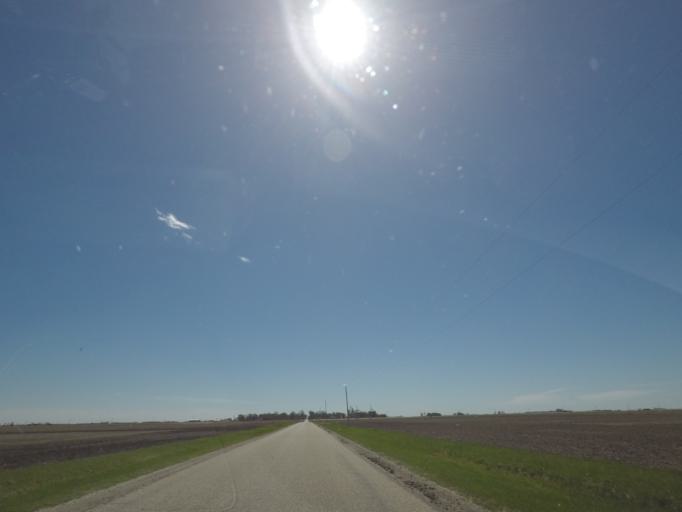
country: US
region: Illinois
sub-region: Logan County
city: Atlanta
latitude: 40.1569
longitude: -89.1935
